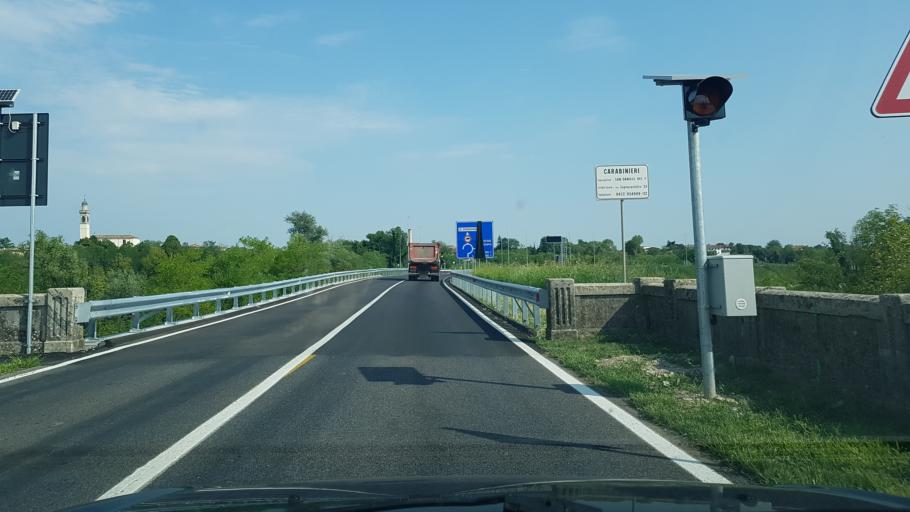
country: IT
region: Friuli Venezia Giulia
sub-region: Provincia di Udine
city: Dignano
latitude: 46.0847
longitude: 12.9302
